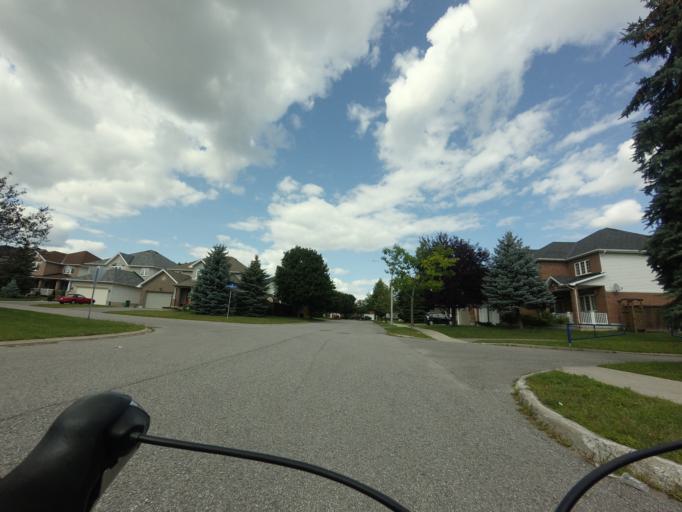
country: CA
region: Ontario
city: Bells Corners
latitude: 45.2947
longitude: -75.8543
